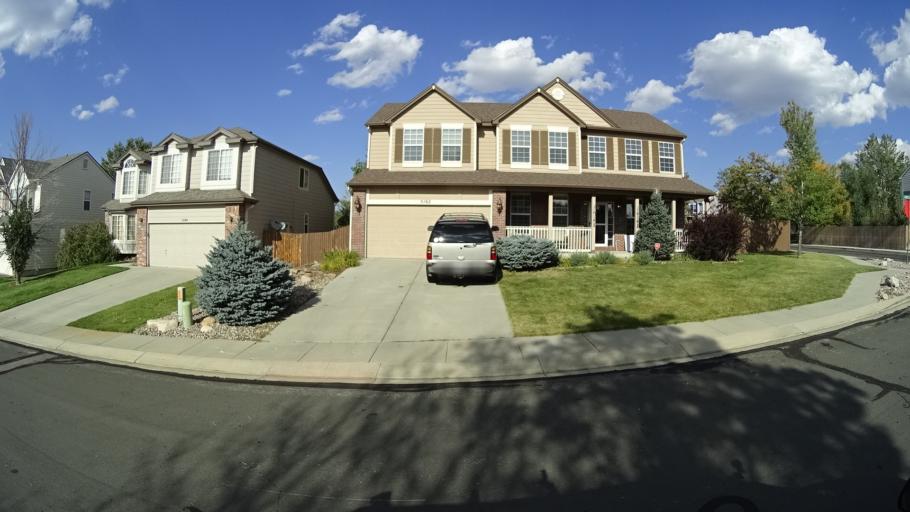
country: US
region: Colorado
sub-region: El Paso County
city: Cimarron Hills
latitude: 38.9117
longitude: -104.7328
